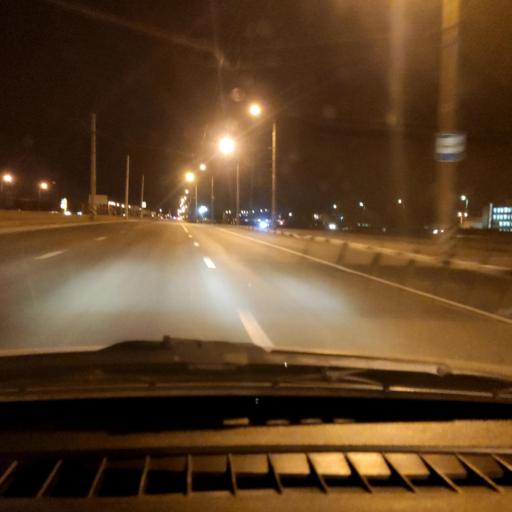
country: RU
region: Samara
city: Podstepki
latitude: 53.5579
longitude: 49.2369
